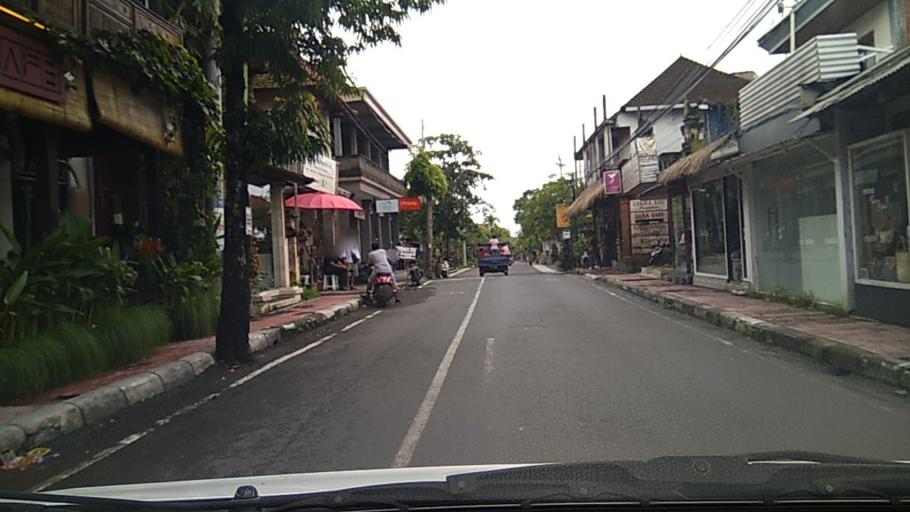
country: ID
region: Bali
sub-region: Kabupaten Gianyar
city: Ubud
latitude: -8.5139
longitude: 115.2641
